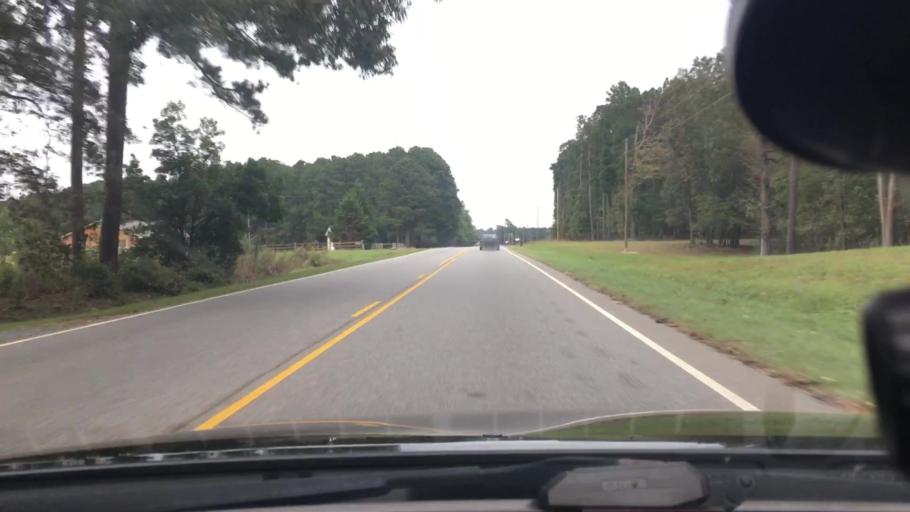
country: US
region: North Carolina
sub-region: Moore County
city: Robbins
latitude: 35.3729
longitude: -79.6717
